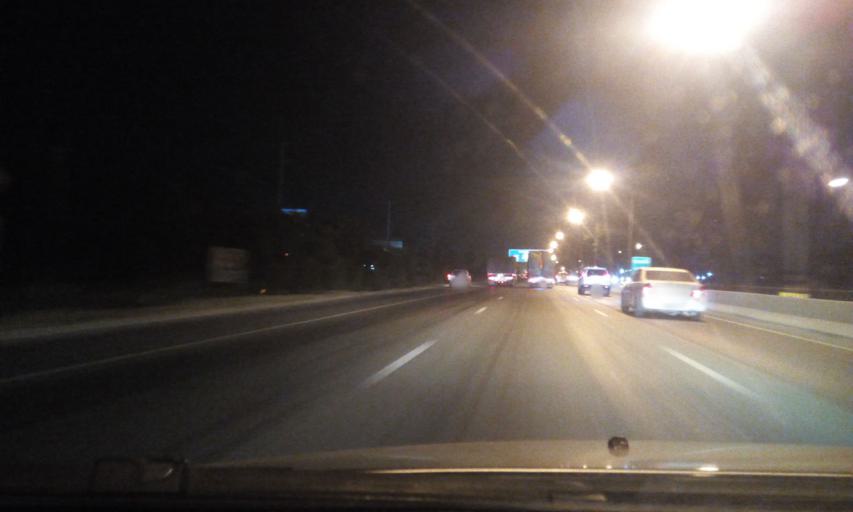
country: TH
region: Ang Thong
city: Chaiyo
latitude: 14.7311
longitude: 100.4550
